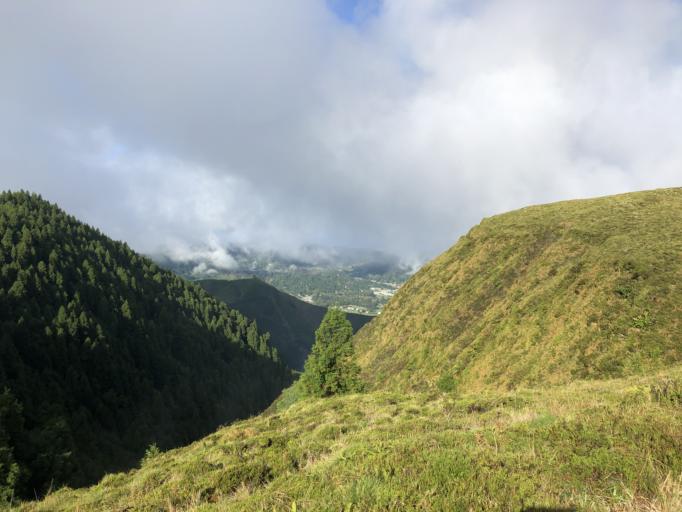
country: PT
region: Azores
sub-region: Ponta Delgada
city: Arrifes
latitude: 37.8400
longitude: -25.7625
